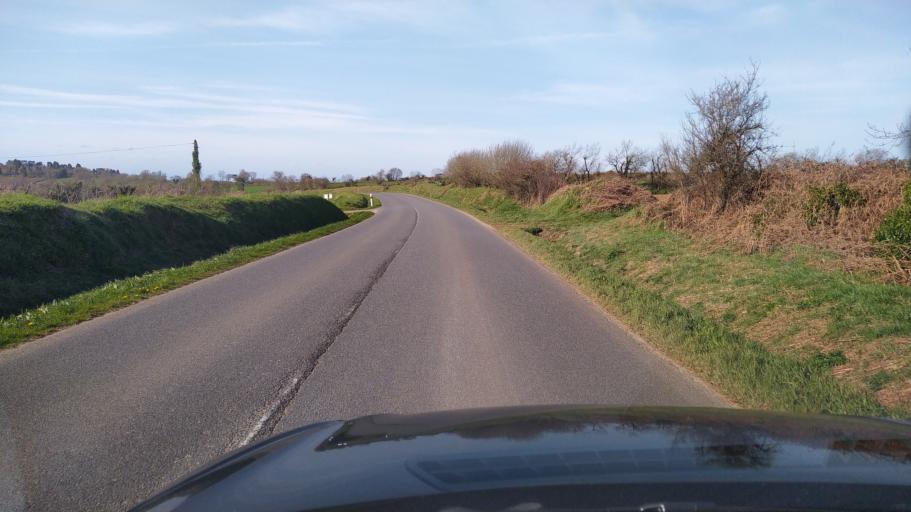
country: FR
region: Brittany
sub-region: Departement du Finistere
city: Lampaul-Guimiliau
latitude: 48.4744
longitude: -4.0221
